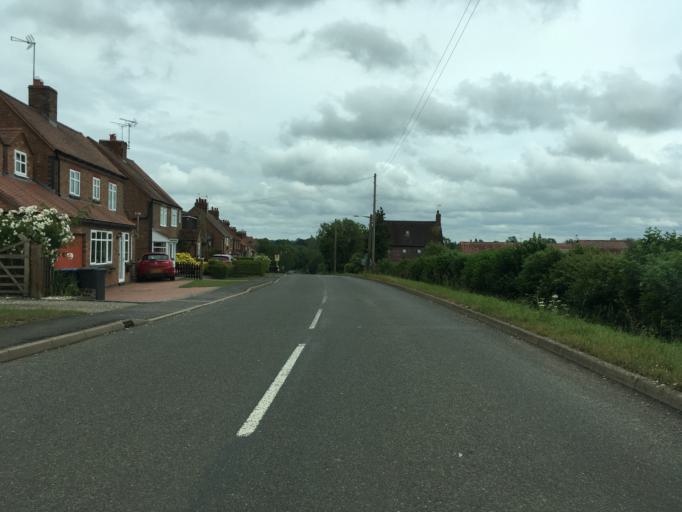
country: GB
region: England
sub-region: Warwickshire
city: Harbury
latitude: 52.2313
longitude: -1.4199
